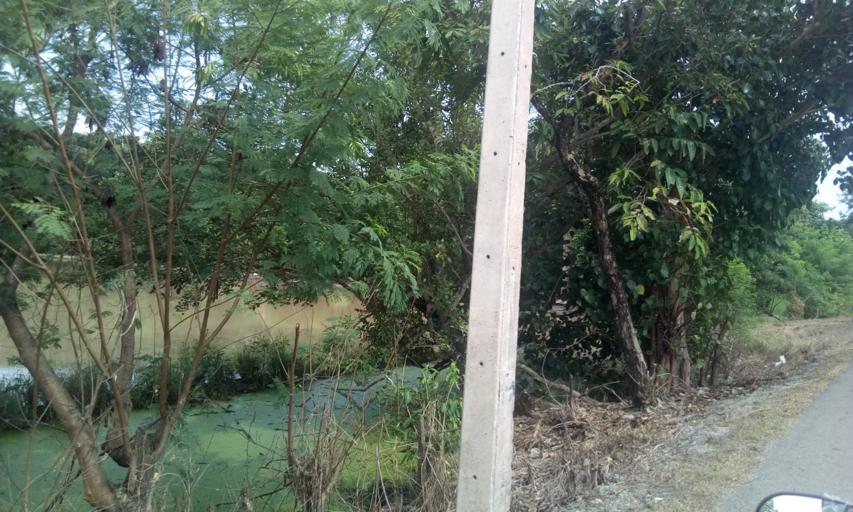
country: TH
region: Pathum Thani
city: Ban Lam Luk Ka
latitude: 14.0215
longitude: 100.8435
